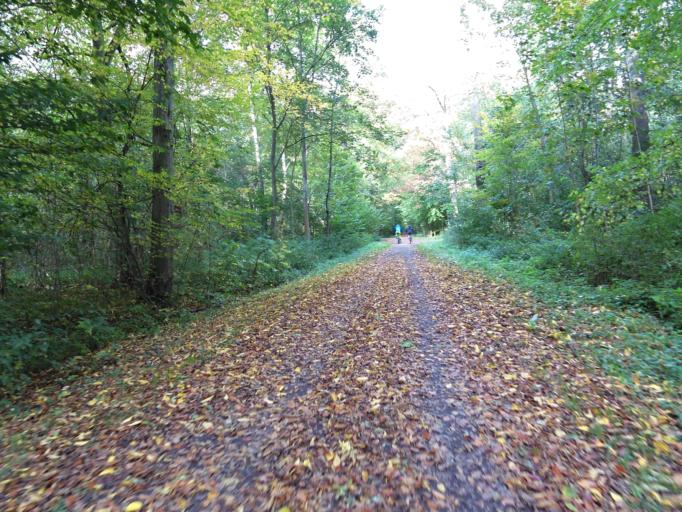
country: DE
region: Saxony
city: Markkleeberg
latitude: 51.2995
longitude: 12.3494
